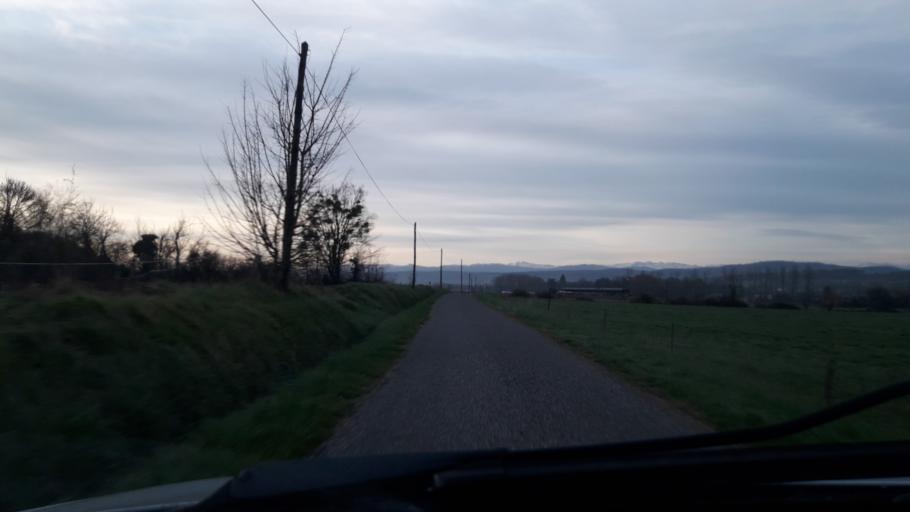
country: FR
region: Midi-Pyrenees
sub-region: Departement de la Haute-Garonne
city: Montesquieu-Volvestre
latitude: 43.1793
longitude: 1.2665
